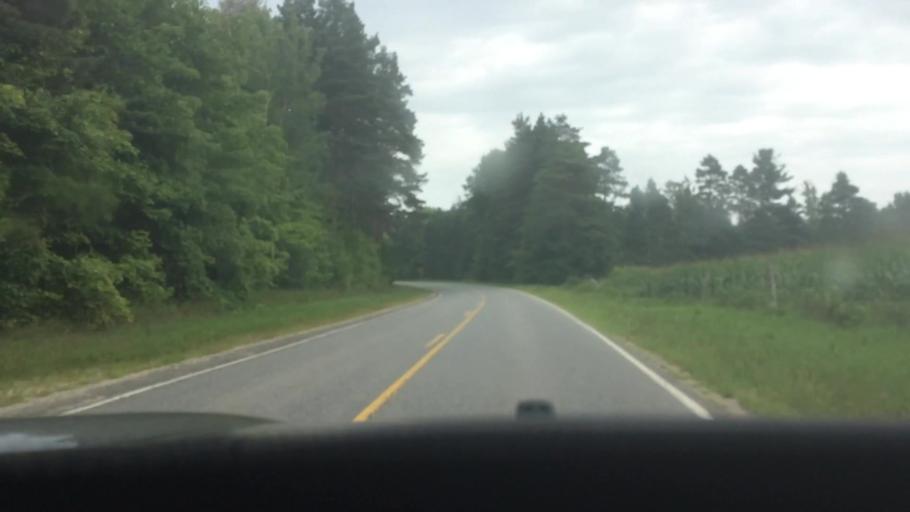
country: US
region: New York
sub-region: St. Lawrence County
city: Hannawa Falls
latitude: 44.6018
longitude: -74.8848
